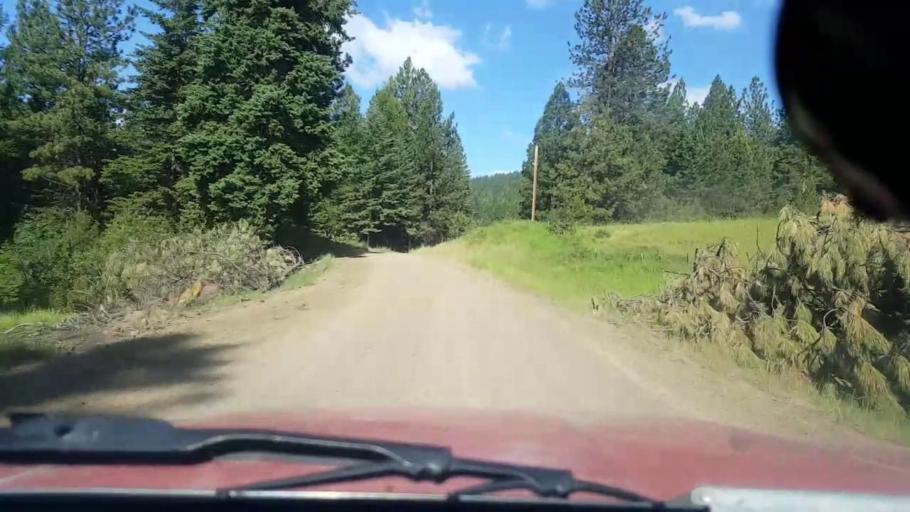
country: US
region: Washington
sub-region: Garfield County
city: Pomeroy
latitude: 46.0370
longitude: -117.4336
